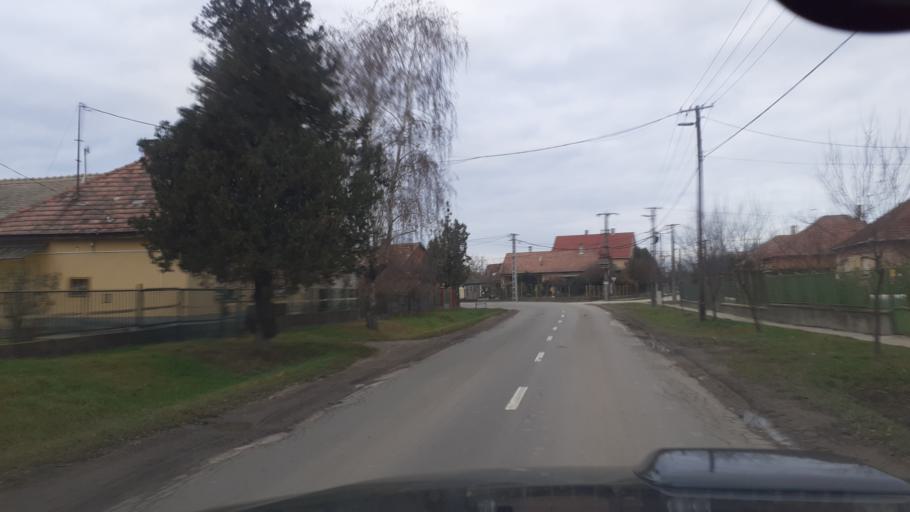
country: HU
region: Bacs-Kiskun
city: Szalkszentmarton
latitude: 46.9723
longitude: 19.0187
